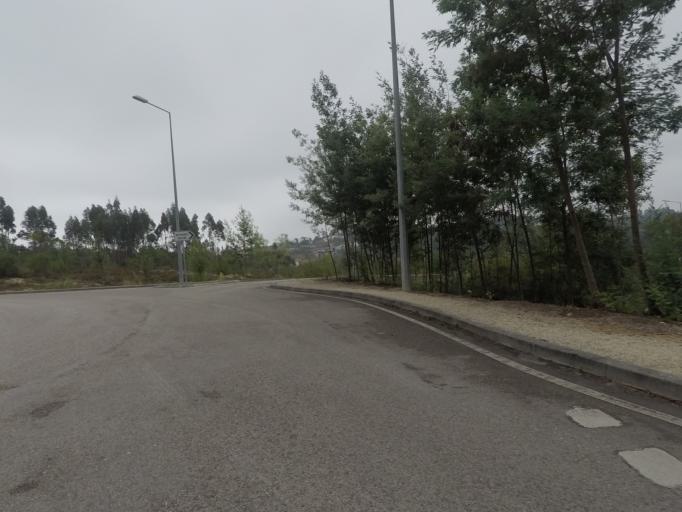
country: PT
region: Coimbra
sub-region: Coimbra
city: Coimbra
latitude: 40.1765
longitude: -8.4565
